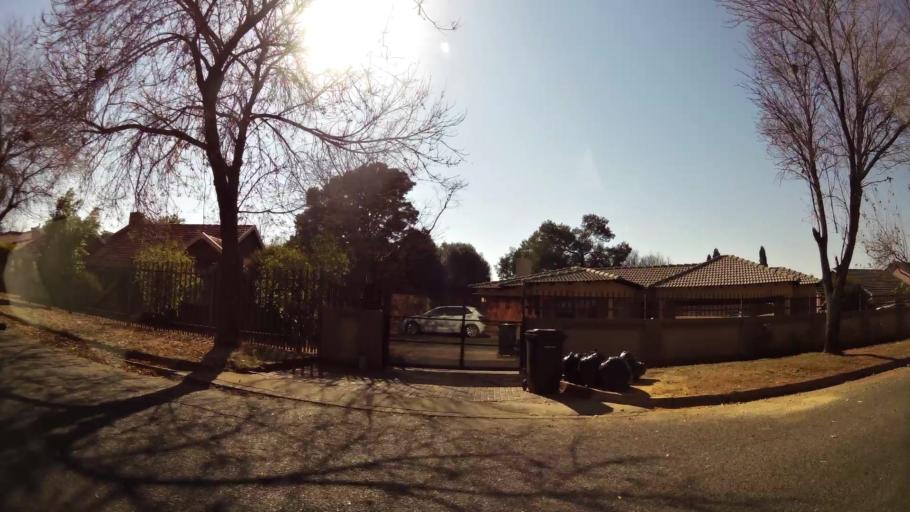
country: ZA
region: Gauteng
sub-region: Ekurhuleni Metropolitan Municipality
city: Tembisa
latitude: -26.0452
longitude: 28.2073
